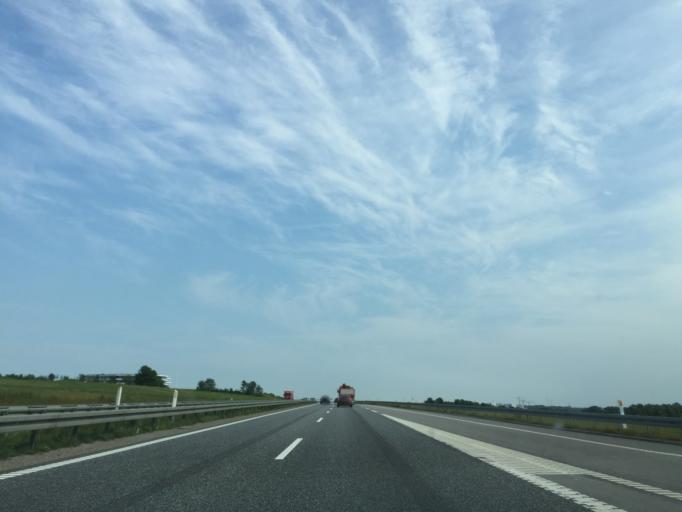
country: DK
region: Central Jutland
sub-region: Arhus Kommune
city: Trige
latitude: 56.2175
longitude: 10.1363
